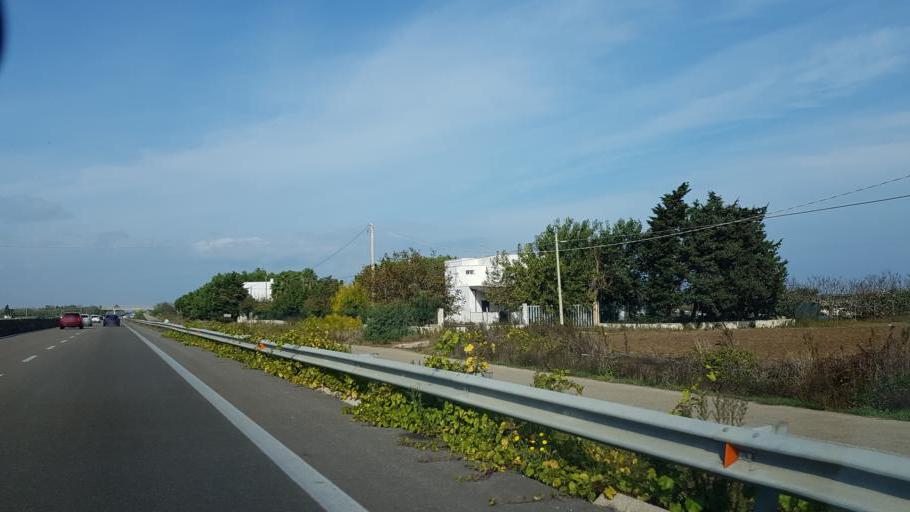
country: IT
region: Apulia
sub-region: Provincia di Brindisi
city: Brindisi
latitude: 40.6847
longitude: 17.8327
